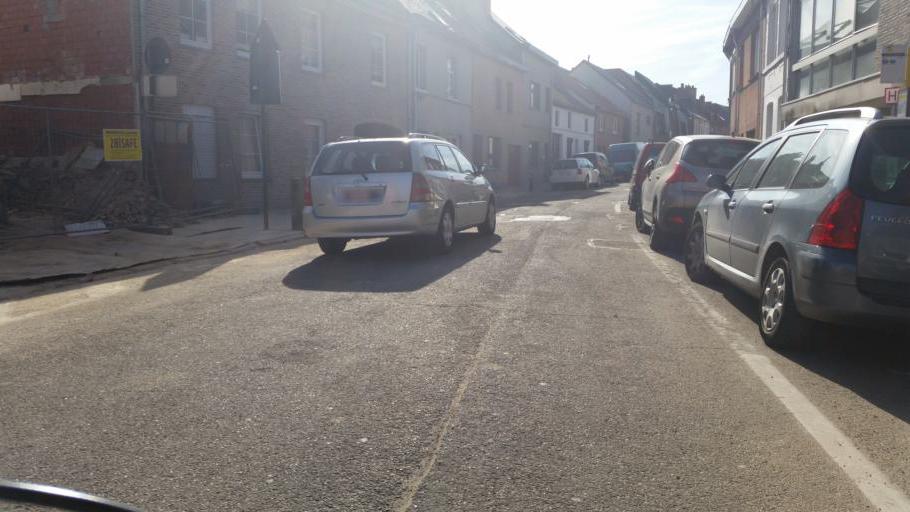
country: BE
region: Flanders
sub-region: Provincie Vlaams-Brabant
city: Tervuren
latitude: 50.8202
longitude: 4.5108
